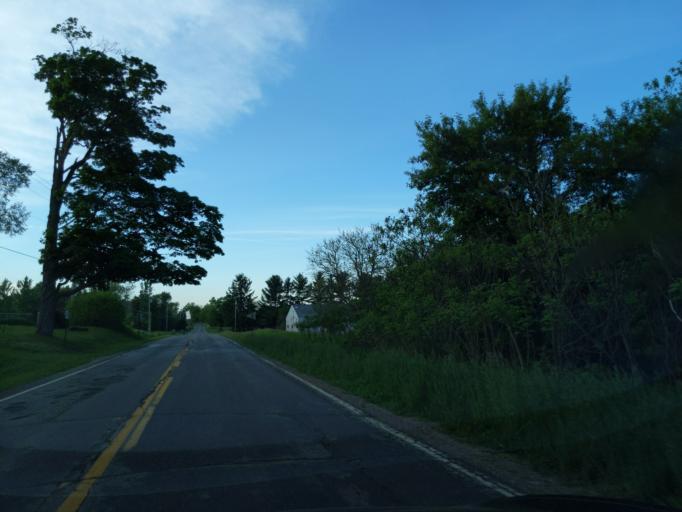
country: US
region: Michigan
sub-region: Ingham County
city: Mason
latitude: 42.5365
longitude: -84.3026
